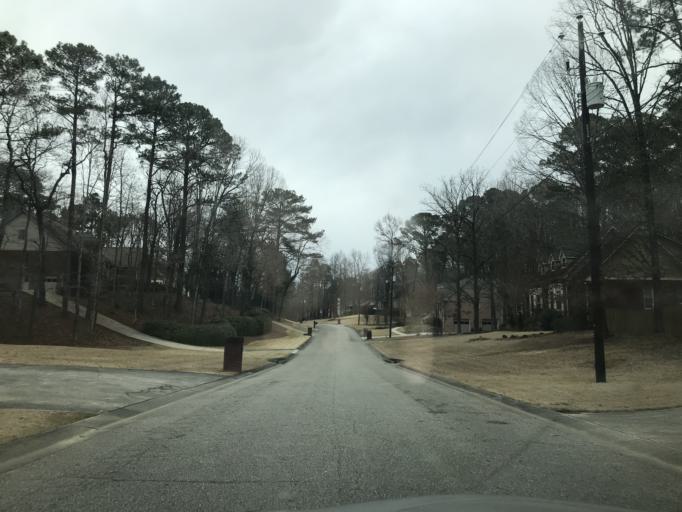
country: US
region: Alabama
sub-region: Shelby County
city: Indian Springs Village
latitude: 33.3813
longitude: -86.7479
